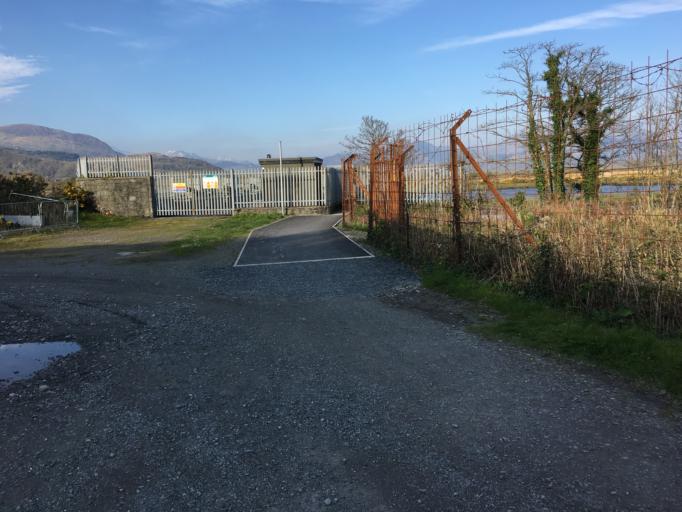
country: GB
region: Wales
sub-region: Gwynedd
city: Porthmadog
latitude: 52.9251
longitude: -4.1252
